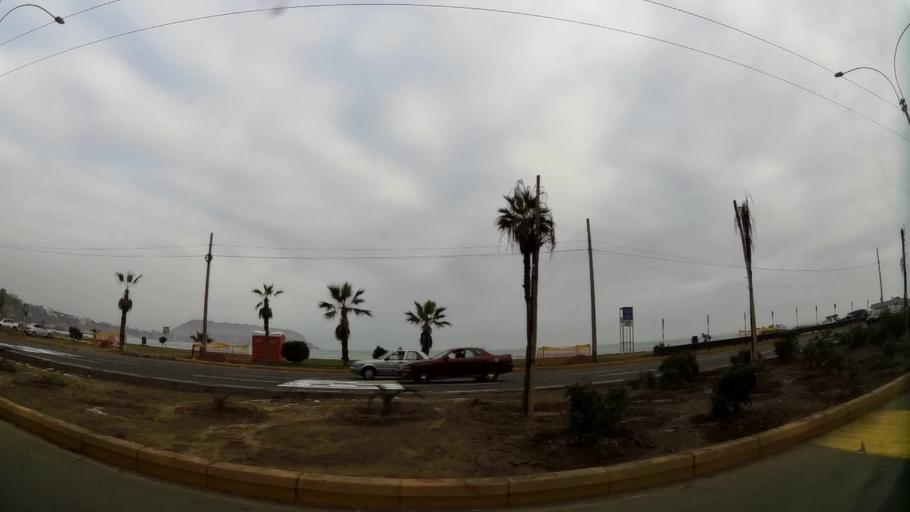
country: PE
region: Lima
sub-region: Lima
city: San Isidro
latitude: -12.1312
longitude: -77.0334
